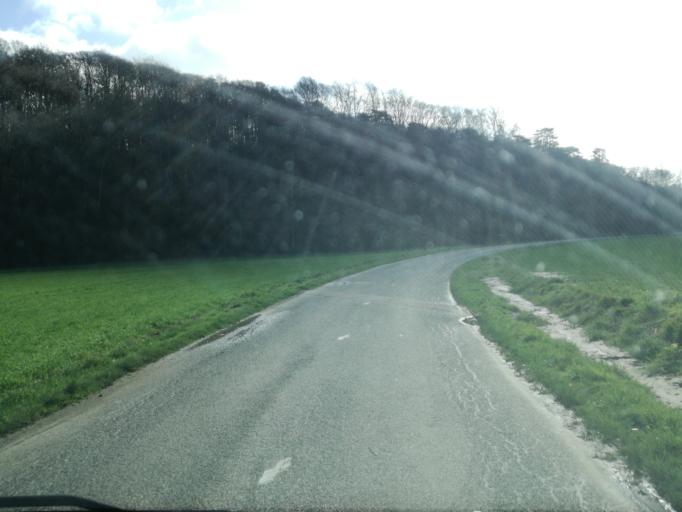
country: FR
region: Haute-Normandie
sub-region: Departement de la Seine-Maritime
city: Yebleron
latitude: 49.6879
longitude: 0.4892
